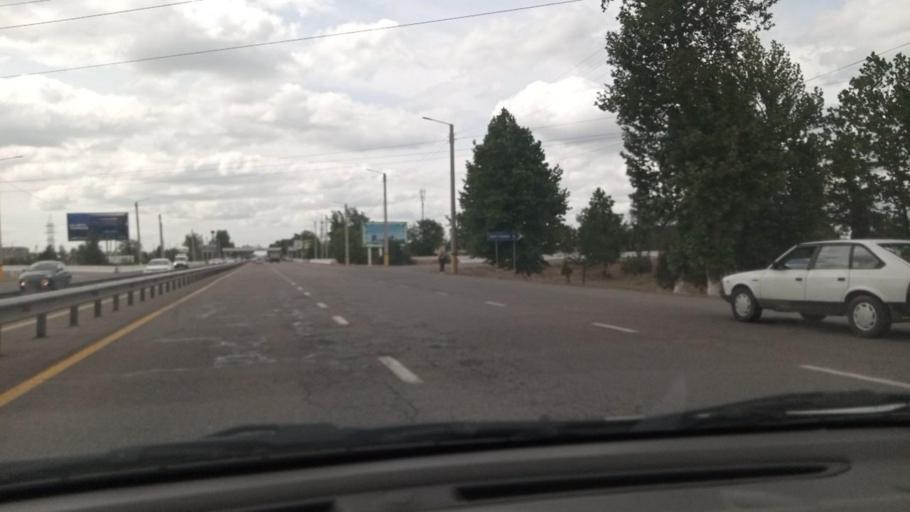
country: UZ
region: Toshkent Shahri
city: Bektemir
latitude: 41.2449
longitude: 69.3959
